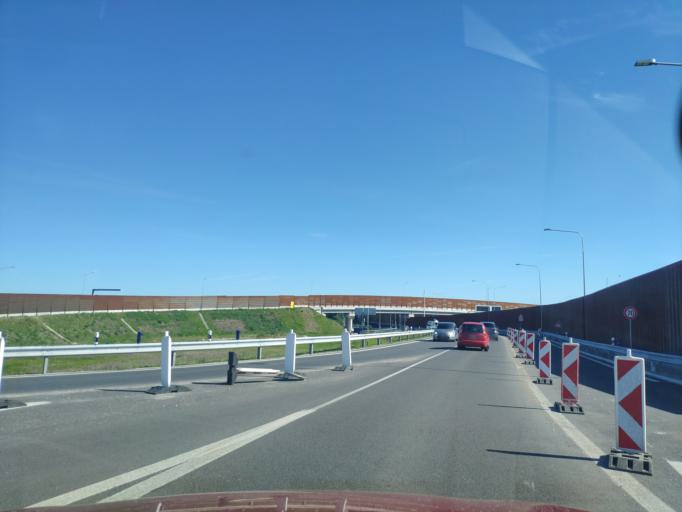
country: SK
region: Bratislavsky
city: Svaty Jur
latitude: 48.2133
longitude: 17.2215
